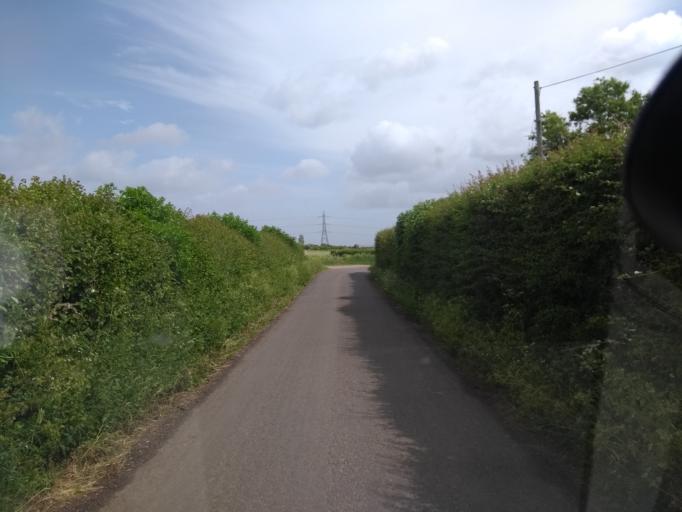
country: GB
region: England
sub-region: Somerset
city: Burnham-on-Sea
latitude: 51.1879
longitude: -3.0795
